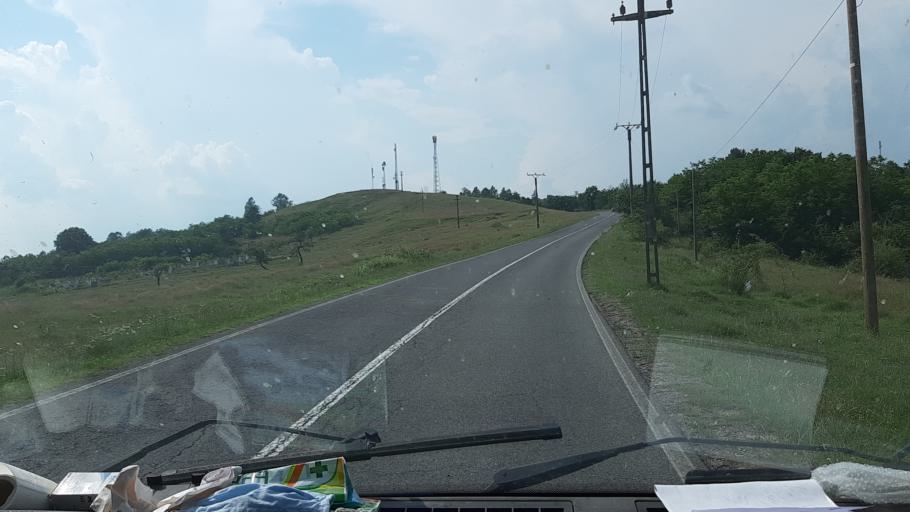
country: RO
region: Caras-Severin
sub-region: Comuna Farliug
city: Farliug
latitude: 45.5155
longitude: 21.8763
